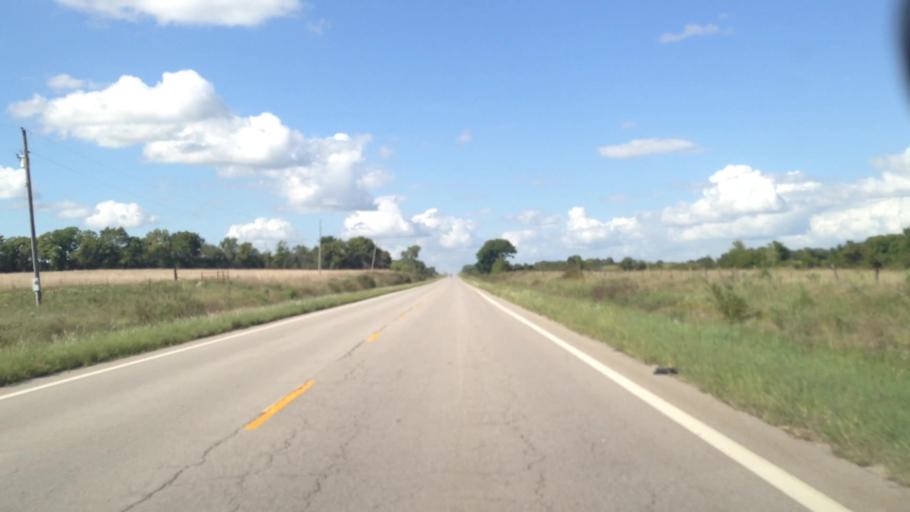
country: US
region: Kansas
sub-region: Neosho County
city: Erie
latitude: 37.7091
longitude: -95.1607
